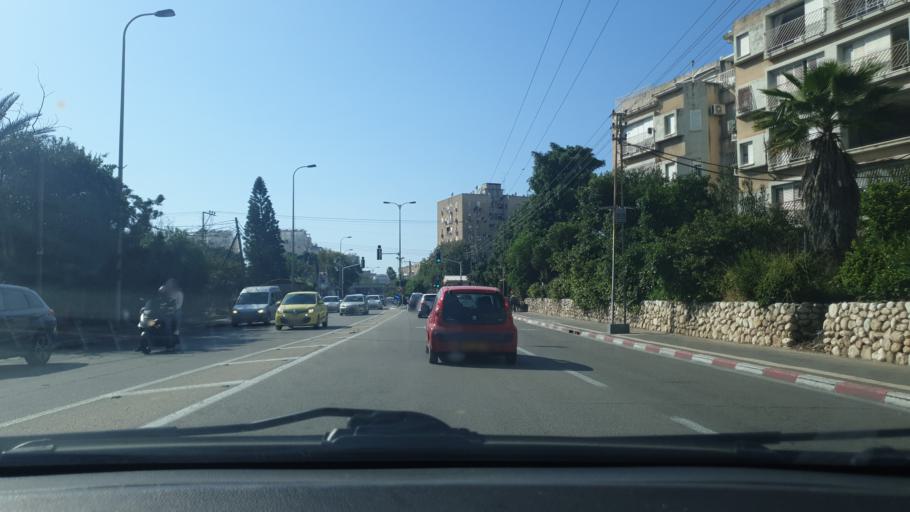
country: IL
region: Tel Aviv
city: Azor
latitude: 32.0448
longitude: 34.8120
